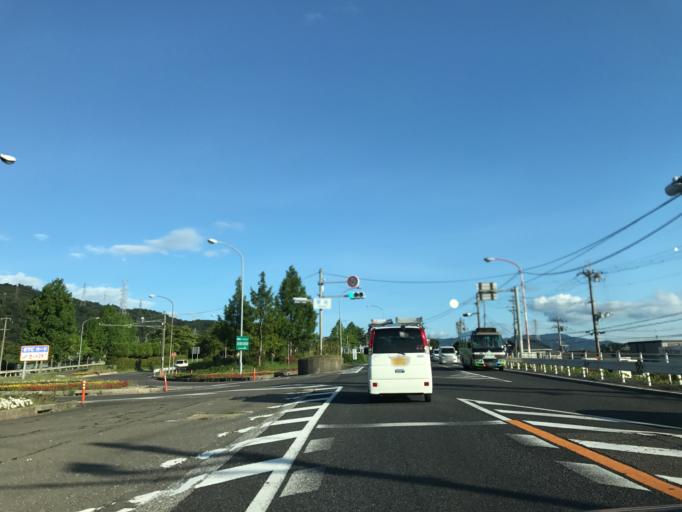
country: JP
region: Shiga Prefecture
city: Hikone
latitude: 35.2622
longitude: 136.2717
